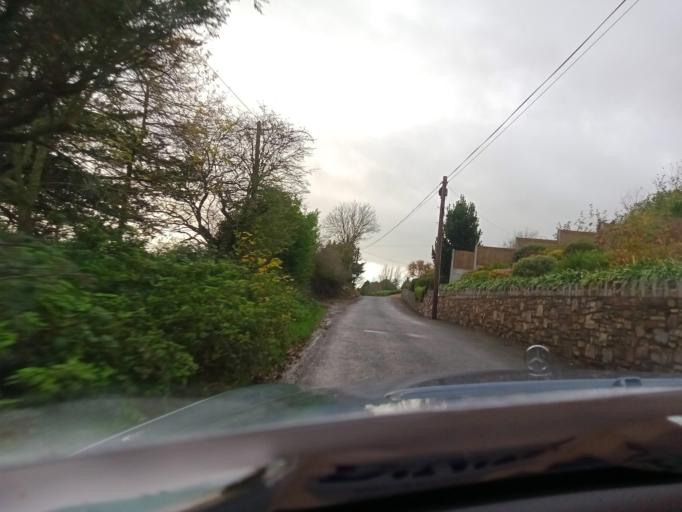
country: IE
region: Leinster
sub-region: Kilkenny
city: Mooncoin
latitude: 52.2714
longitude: -7.1846
